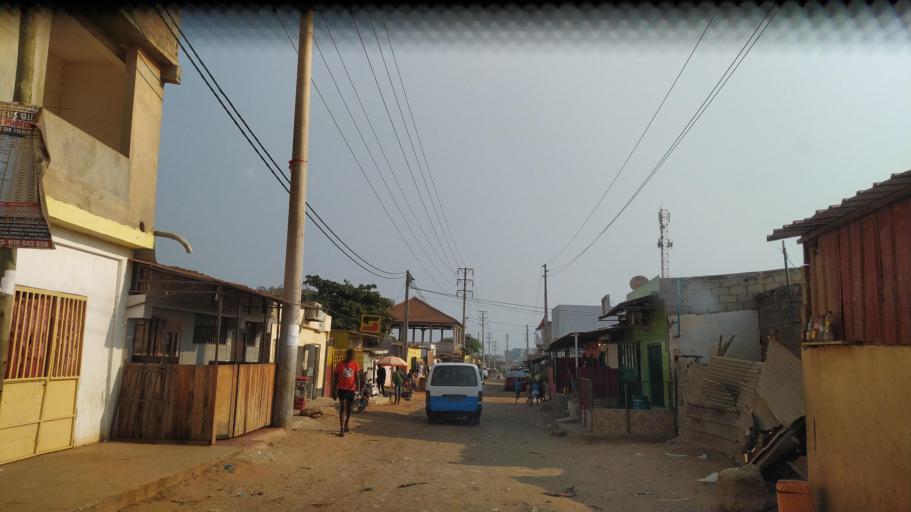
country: AO
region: Luanda
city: Luanda
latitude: -8.8680
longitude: 13.2009
